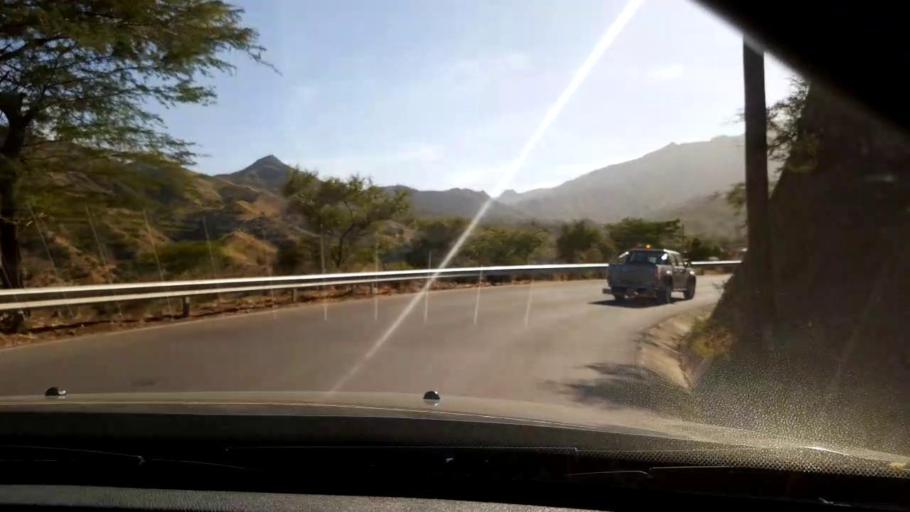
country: CV
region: Sao Lourenco dos Orgaos
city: Joao Teves
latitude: 15.0722
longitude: -23.5674
